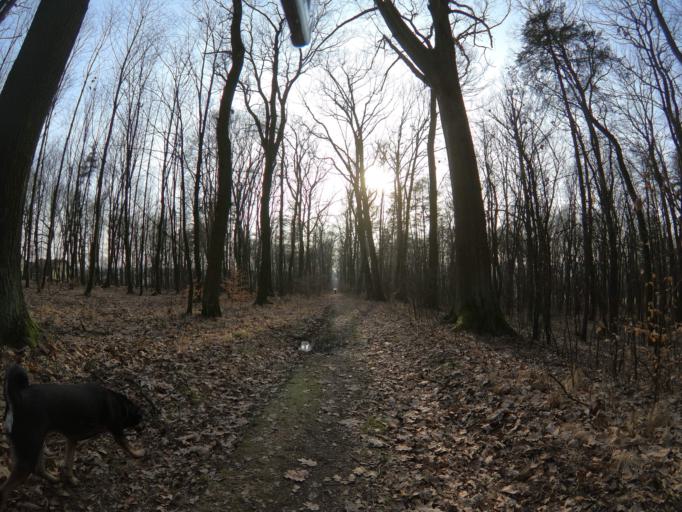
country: PL
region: Silesian Voivodeship
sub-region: Powiat raciborski
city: Pogrzebien
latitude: 50.0812
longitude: 18.2602
